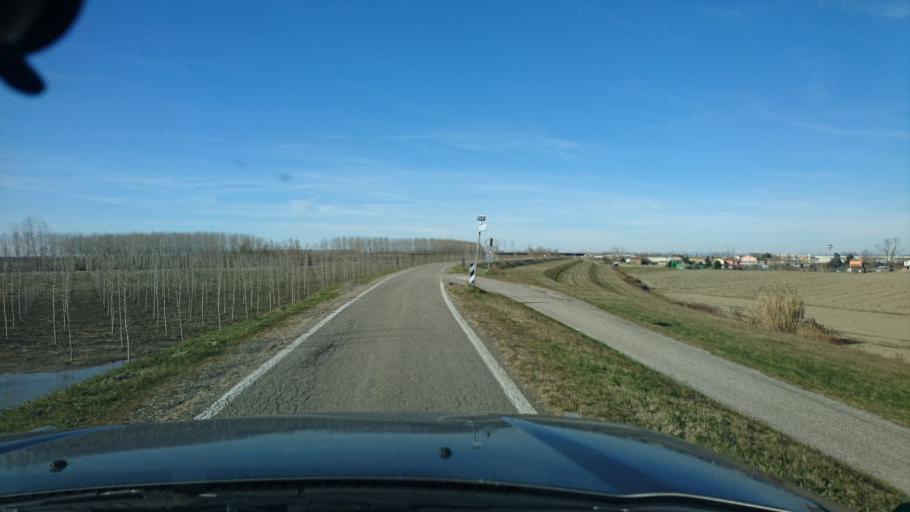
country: IT
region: Veneto
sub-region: Provincia di Rovigo
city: Ariano
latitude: 44.9345
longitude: 12.1314
